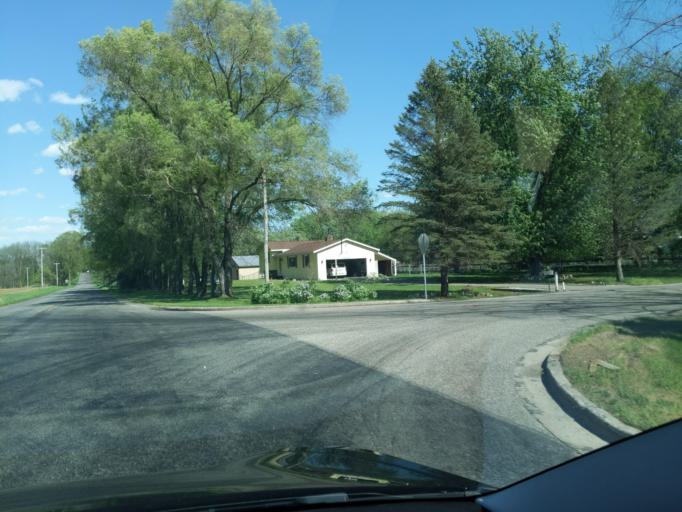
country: US
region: Michigan
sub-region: Barry County
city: Middleville
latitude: 42.7981
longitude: -85.4087
